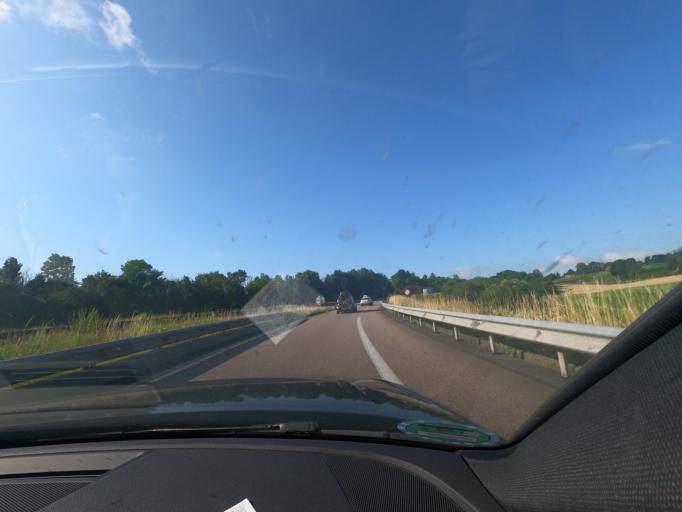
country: FR
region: Haute-Normandie
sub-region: Departement de la Seine-Maritime
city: Neufchatel-en-Bray
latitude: 49.7537
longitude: 1.4831
